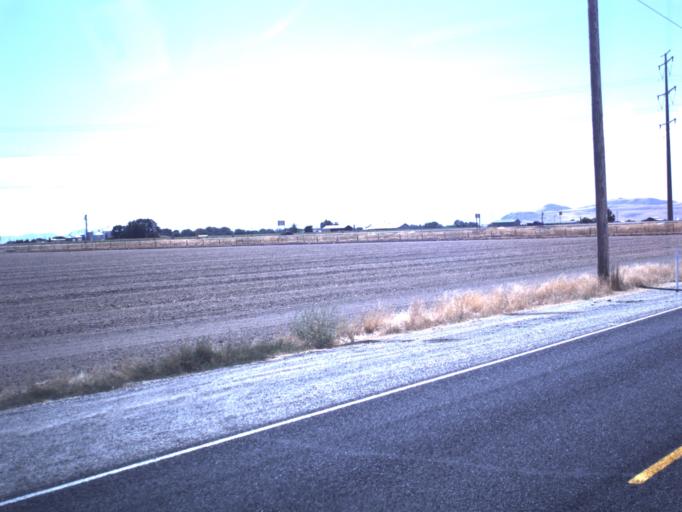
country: US
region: Utah
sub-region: Box Elder County
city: Honeyville
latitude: 41.6350
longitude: -112.0961
